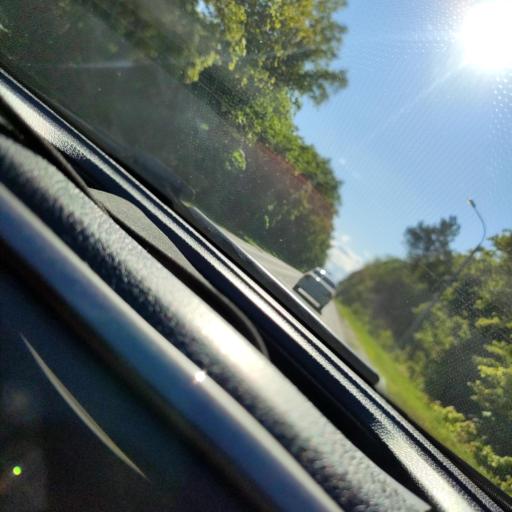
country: RU
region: Samara
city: Tol'yatti
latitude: 53.4735
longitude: 49.3971
